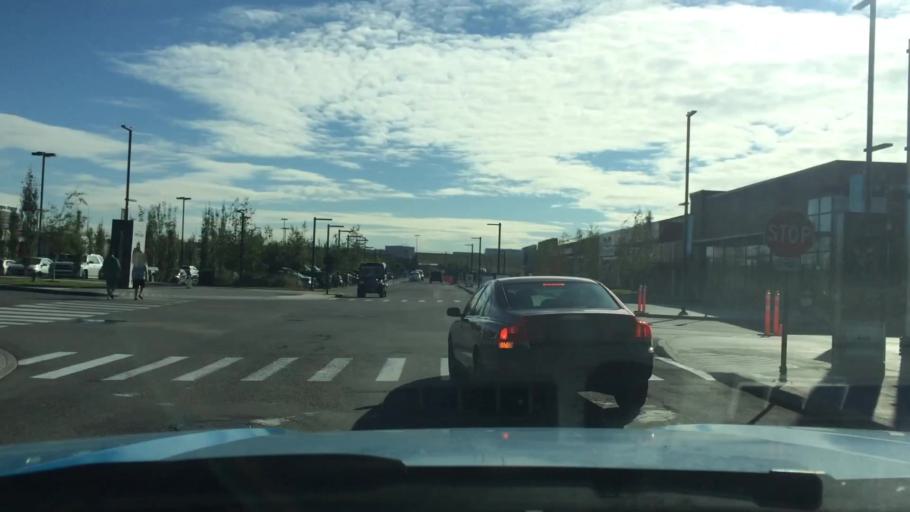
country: CA
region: Alberta
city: Calgary
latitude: 51.1095
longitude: -114.0419
